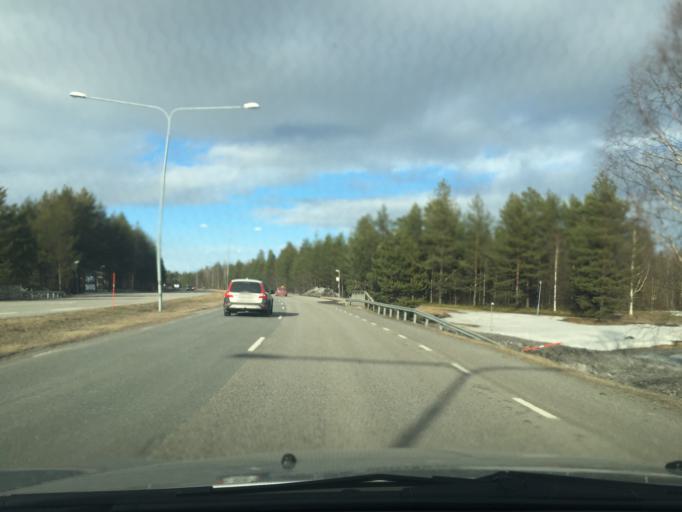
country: SE
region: Norrbotten
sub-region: Lulea Kommun
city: Lulea
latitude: 65.5857
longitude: 22.2216
